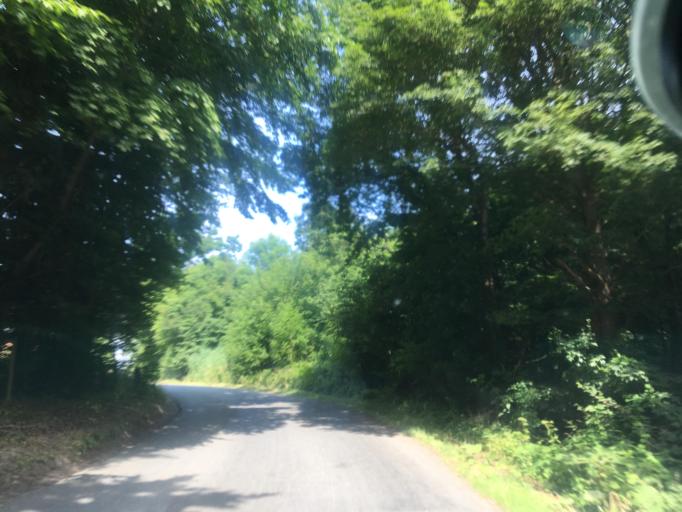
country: DK
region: Zealand
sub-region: Faxe Kommune
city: Ronnede
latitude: 55.1954
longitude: 12.0626
